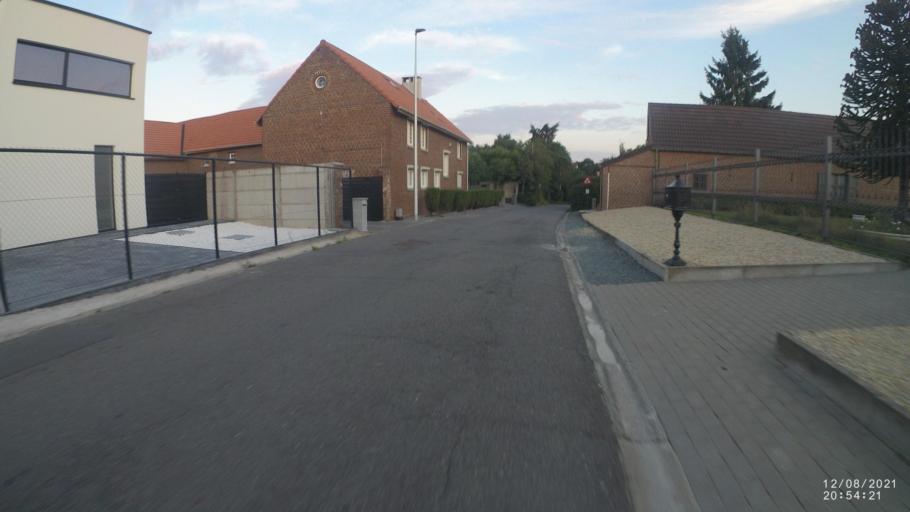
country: BE
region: Flanders
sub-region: Provincie Vlaams-Brabant
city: Dilbeek
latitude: 50.8769
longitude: 4.2649
